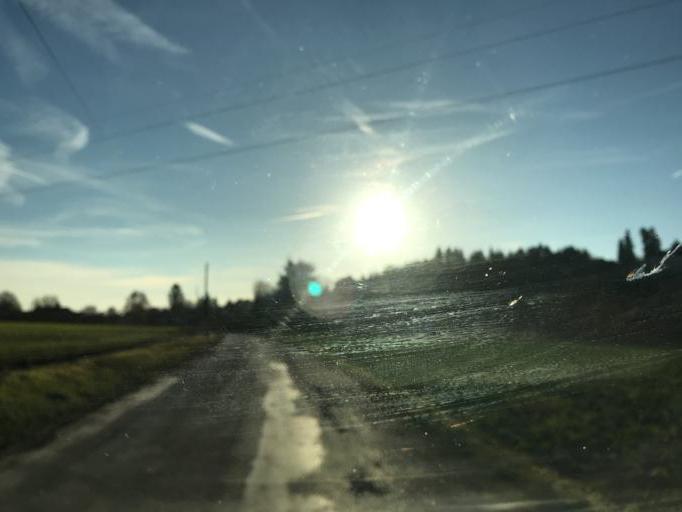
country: FR
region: Rhone-Alpes
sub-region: Departement de l'Ain
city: Meximieux
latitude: 45.9145
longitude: 5.2112
